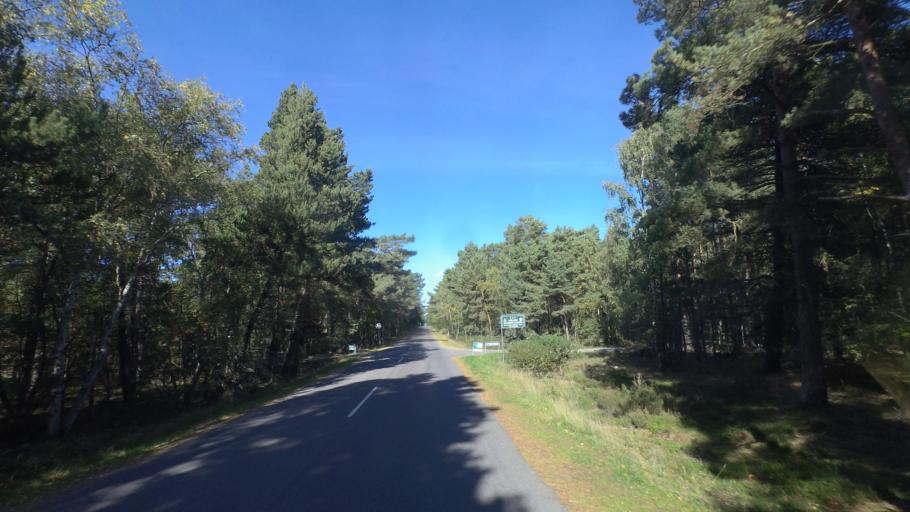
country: DK
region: Capital Region
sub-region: Bornholm Kommune
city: Nexo
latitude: 54.9959
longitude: 15.0771
